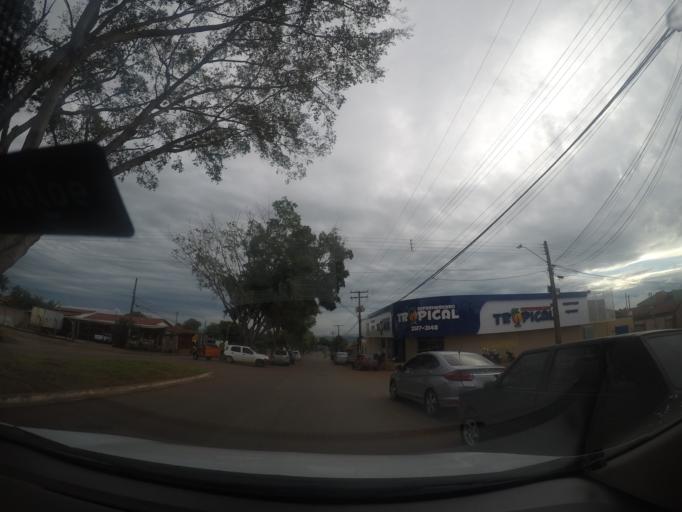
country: BR
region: Goias
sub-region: Goiania
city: Goiania
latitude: -16.6060
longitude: -49.3094
